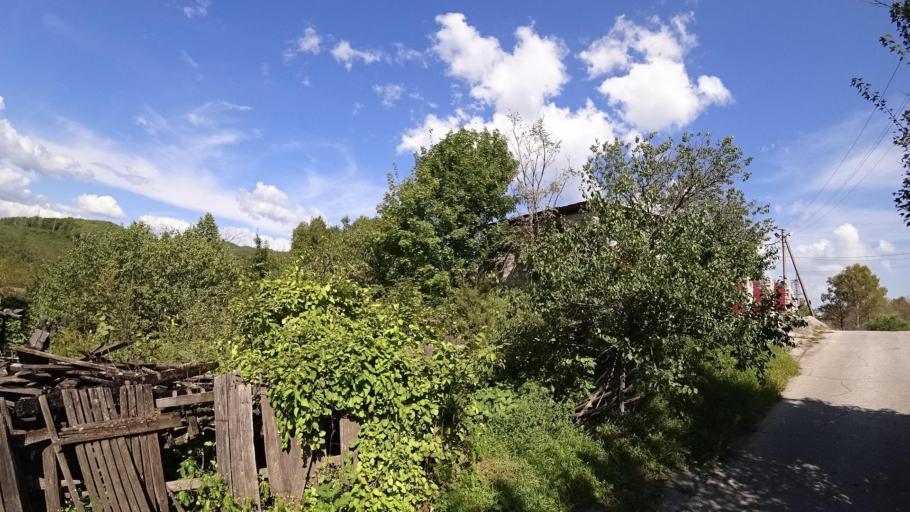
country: RU
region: Jewish Autonomous Oblast
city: Londoko
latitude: 49.0174
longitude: 131.8857
